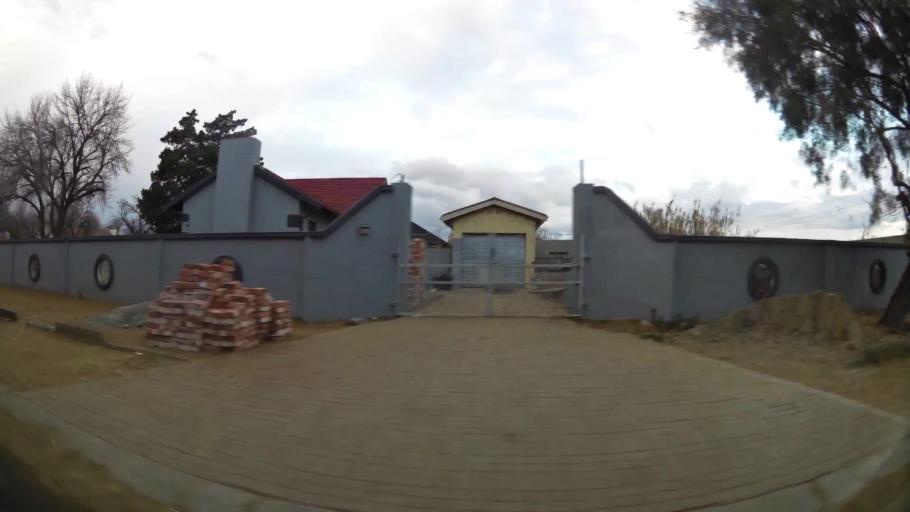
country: ZA
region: Orange Free State
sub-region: Lejweleputswa District Municipality
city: Welkom
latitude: -27.9672
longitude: 26.7703
